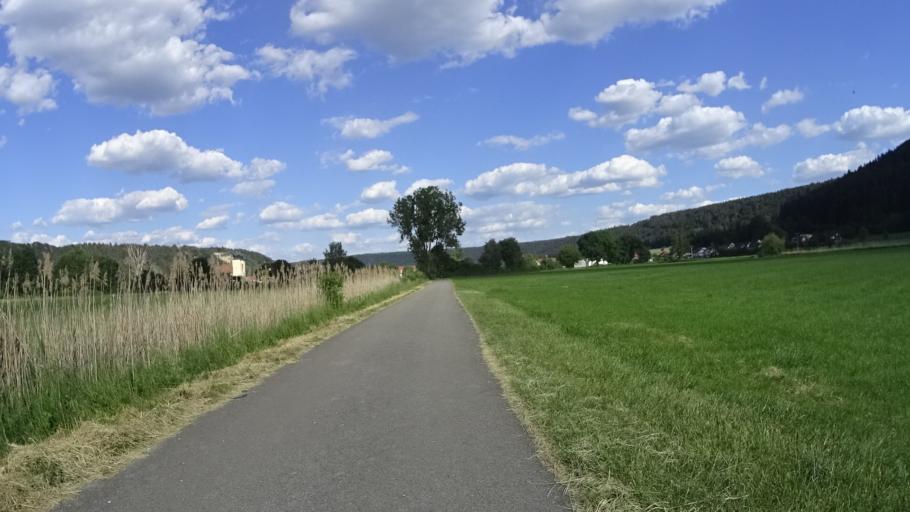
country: DE
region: Bavaria
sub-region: Upper Palatinate
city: Dietfurt
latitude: 49.0202
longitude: 11.5126
